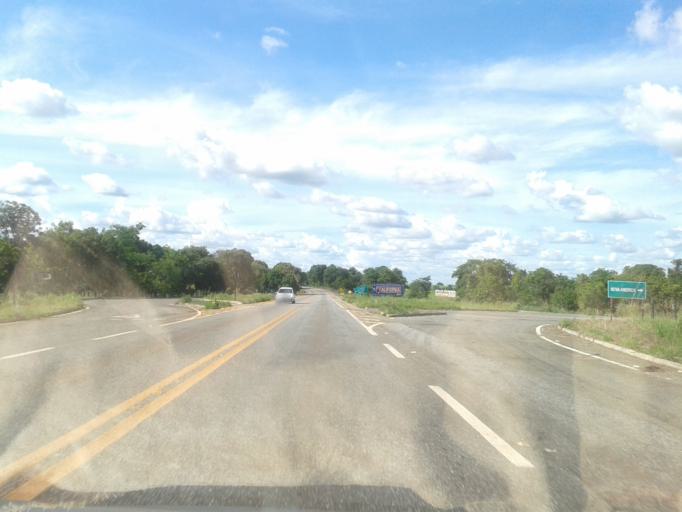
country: BR
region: Goias
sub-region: Mozarlandia
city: Mozarlandia
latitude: -14.8060
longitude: -50.5332
